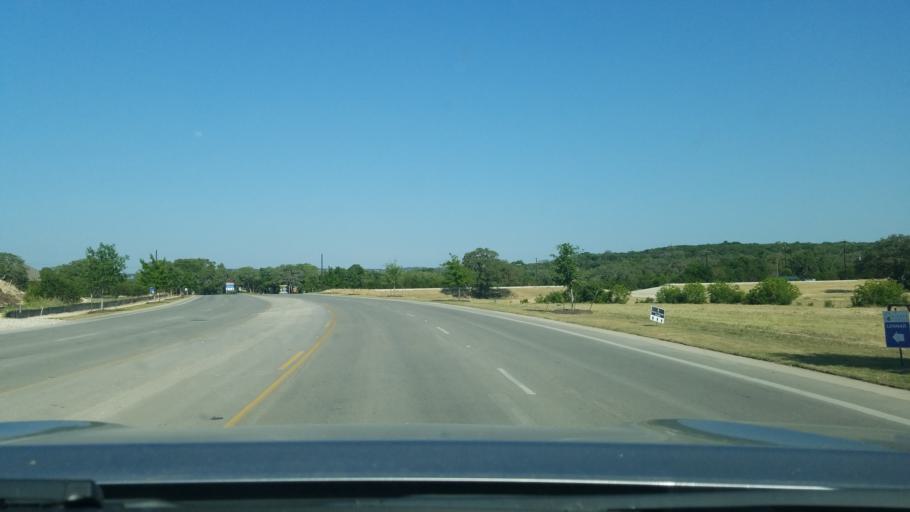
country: US
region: Texas
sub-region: Comal County
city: Bulverde
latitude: 29.7713
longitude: -98.4158
